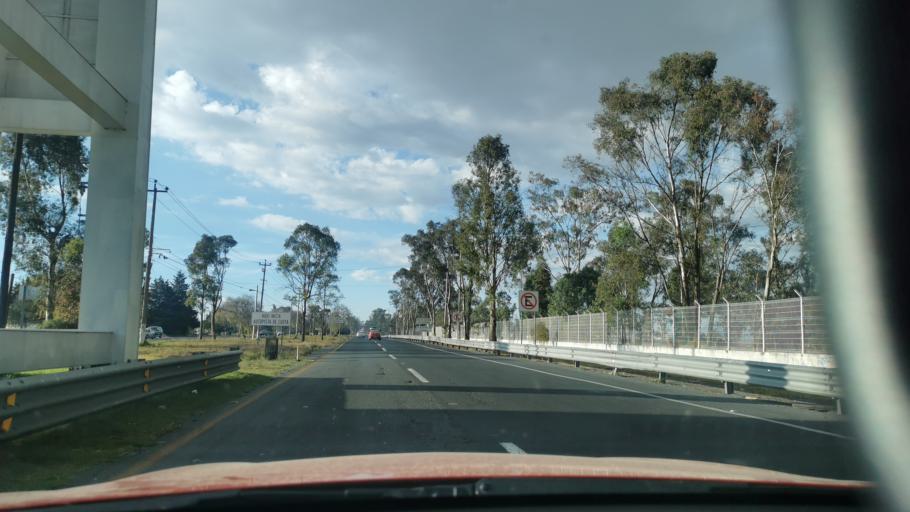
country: MX
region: Mexico
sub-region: Toluca
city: Barrio de Jesus Fraccion Primera
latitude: 19.3684
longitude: -99.6940
